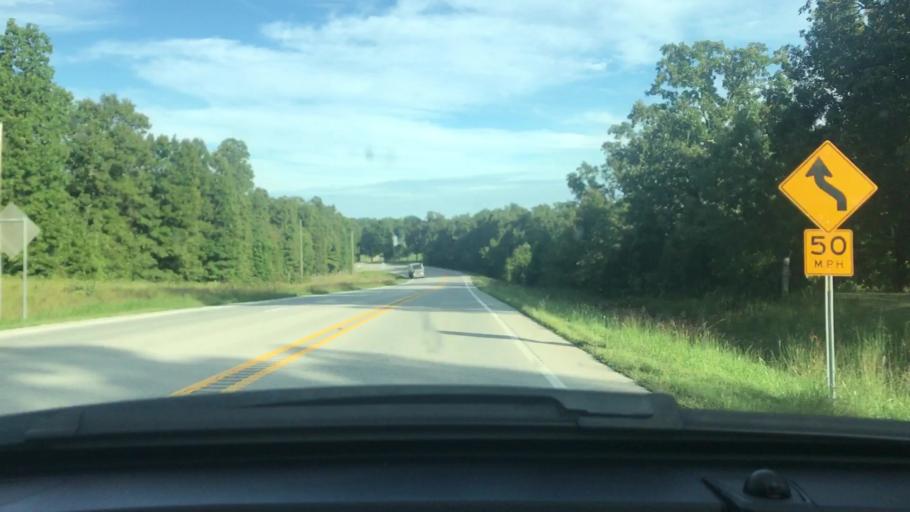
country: US
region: Arkansas
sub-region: Sharp County
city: Cherokee Village
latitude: 36.2728
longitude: -91.3724
